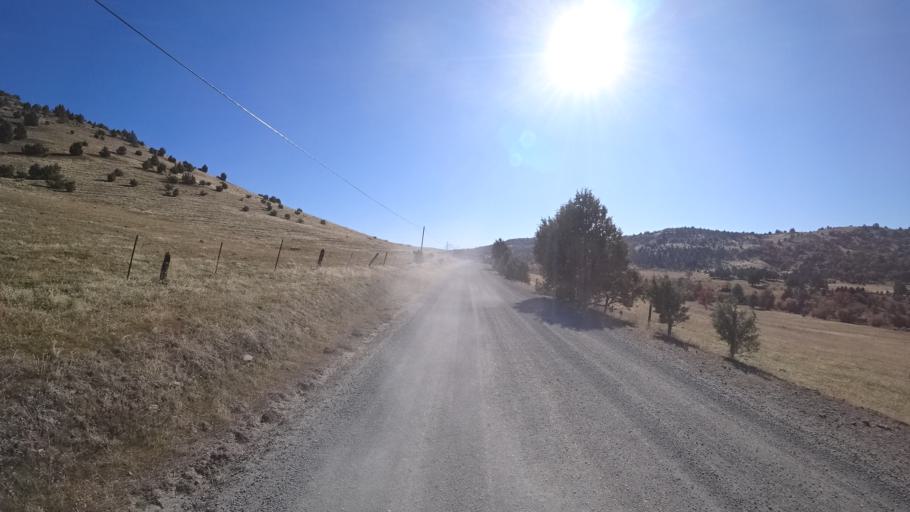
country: US
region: California
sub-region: Siskiyou County
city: Montague
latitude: 41.7998
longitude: -122.3681
